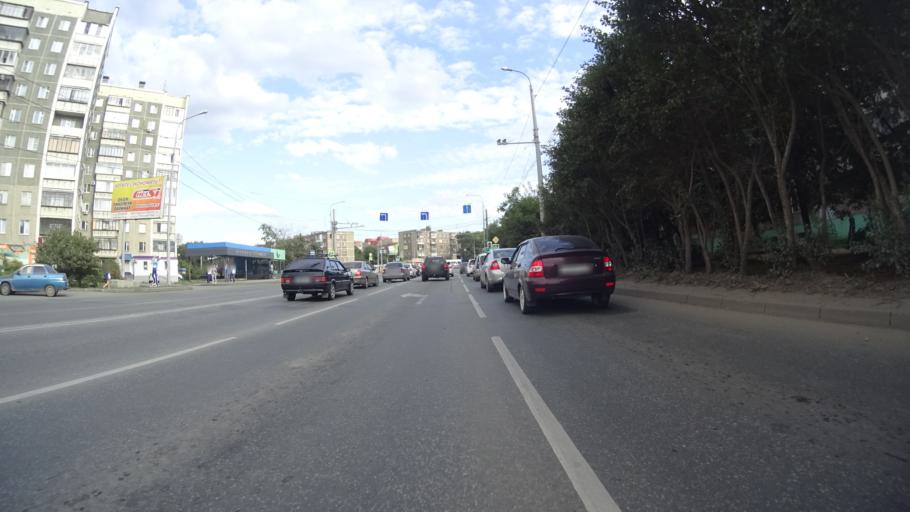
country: RU
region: Chelyabinsk
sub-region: Gorod Chelyabinsk
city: Chelyabinsk
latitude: 55.1991
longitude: 61.3311
